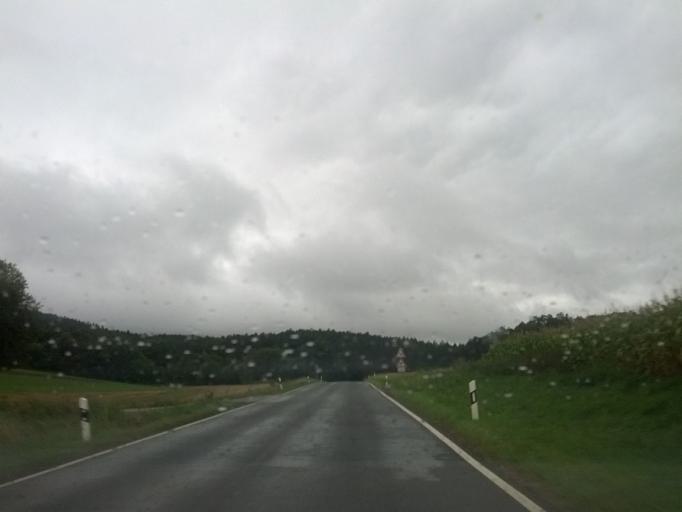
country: DE
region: Thuringia
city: Tabarz
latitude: 50.8912
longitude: 10.5008
